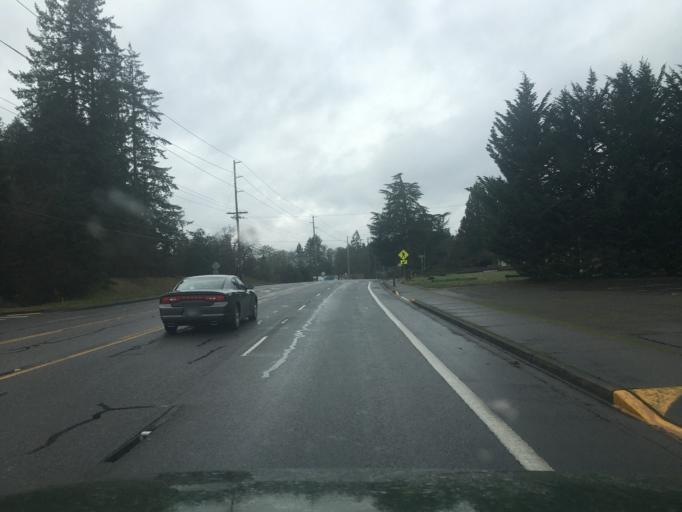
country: US
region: Washington
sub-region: Thurston County
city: Tanglewilde-Thompson Place
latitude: 47.0416
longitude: -122.7870
